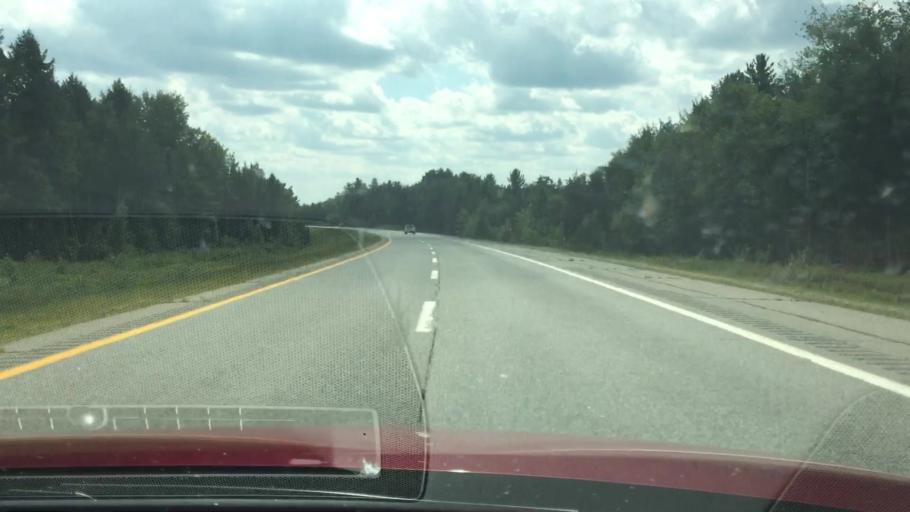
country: US
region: Maine
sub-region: Penobscot County
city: Howland
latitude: 45.2734
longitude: -68.6776
